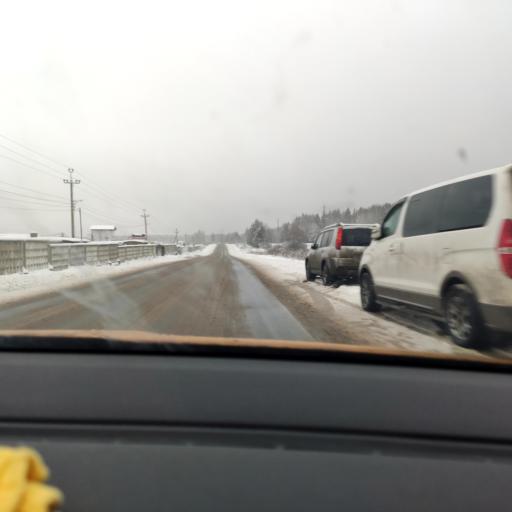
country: RU
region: Moskovskaya
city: Yershovo
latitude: 55.7891
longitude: 36.8480
